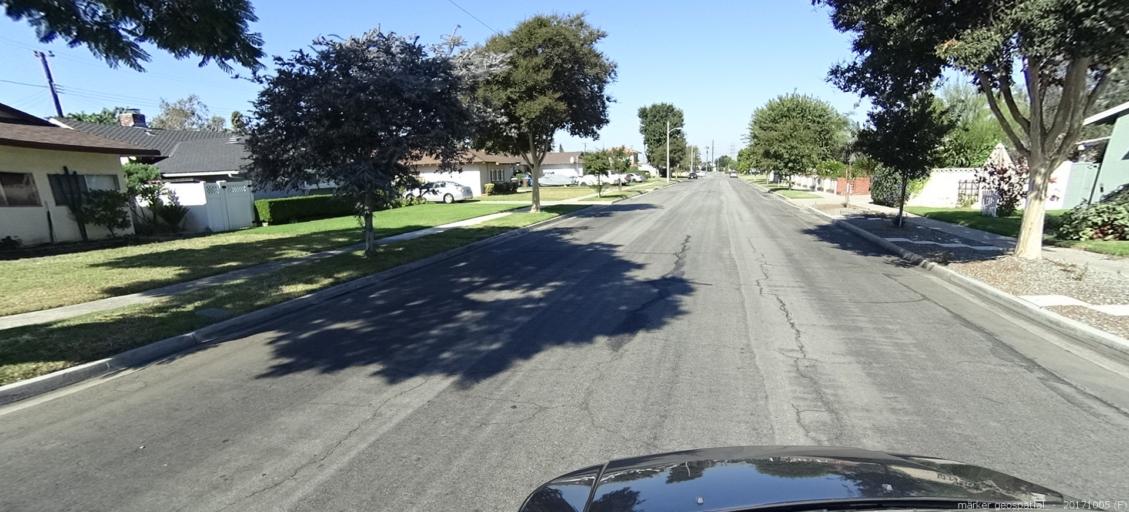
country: US
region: California
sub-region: Orange County
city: Stanton
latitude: 33.7988
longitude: -117.9807
